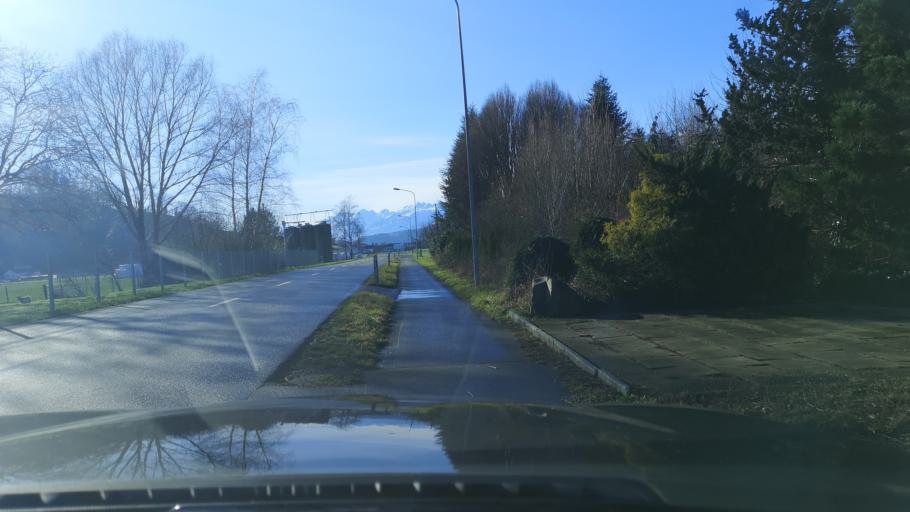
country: AT
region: Vorarlberg
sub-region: Politischer Bezirk Feldkirch
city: Koblach
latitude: 47.3432
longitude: 9.5880
